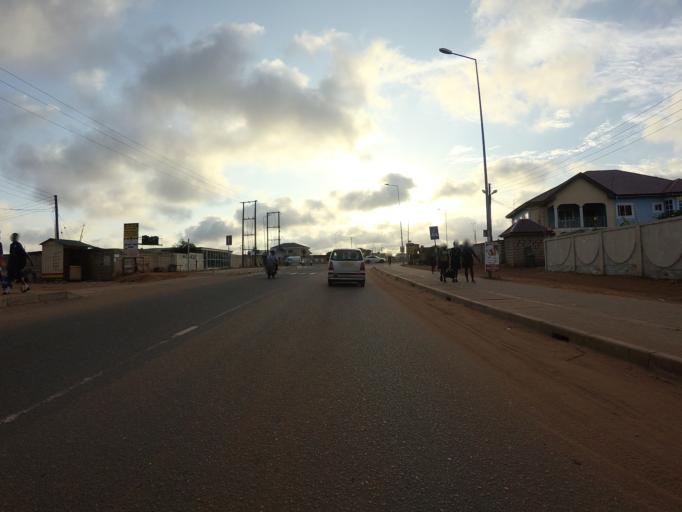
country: GH
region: Greater Accra
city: Teshi Old Town
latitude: 5.5957
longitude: -0.1337
